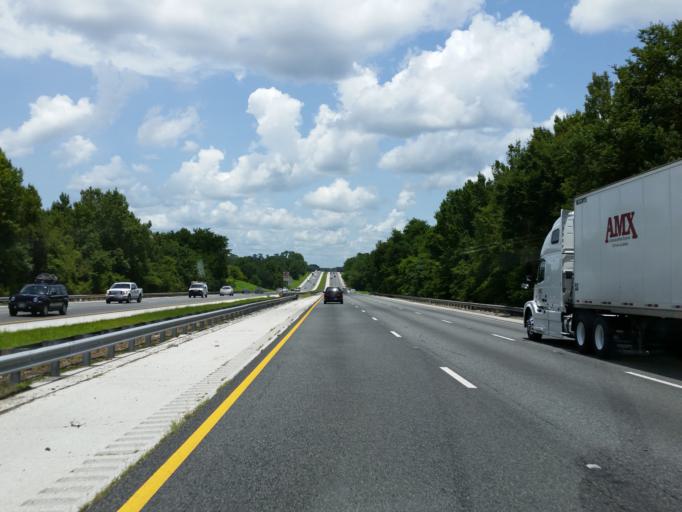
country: US
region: Florida
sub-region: Marion County
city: Citra
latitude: 29.4365
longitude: -82.2644
